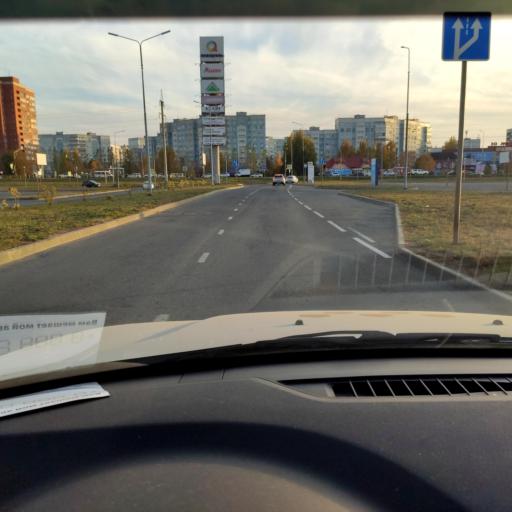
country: RU
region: Samara
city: Tol'yatti
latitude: 53.5501
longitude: 49.3421
